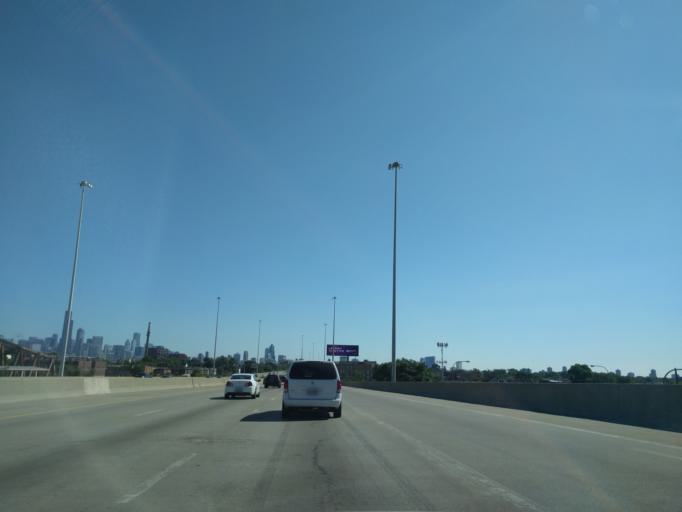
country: US
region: Illinois
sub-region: Cook County
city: Chicago
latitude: 41.8382
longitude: -87.6656
